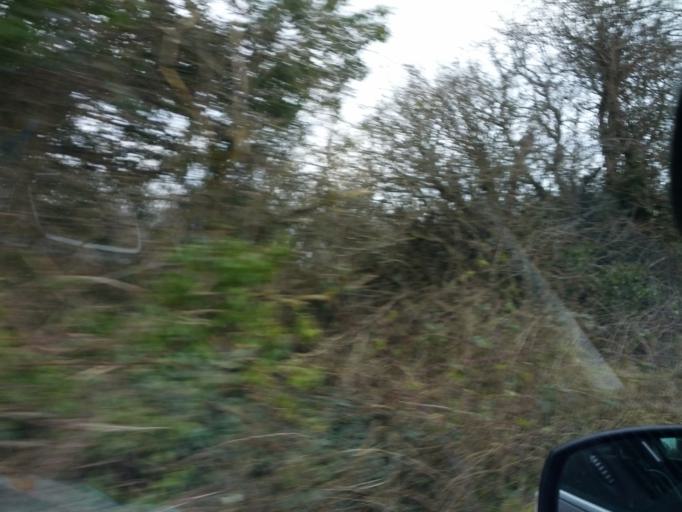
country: IE
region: Connaught
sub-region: County Galway
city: Gort
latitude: 53.1776
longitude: -8.8439
